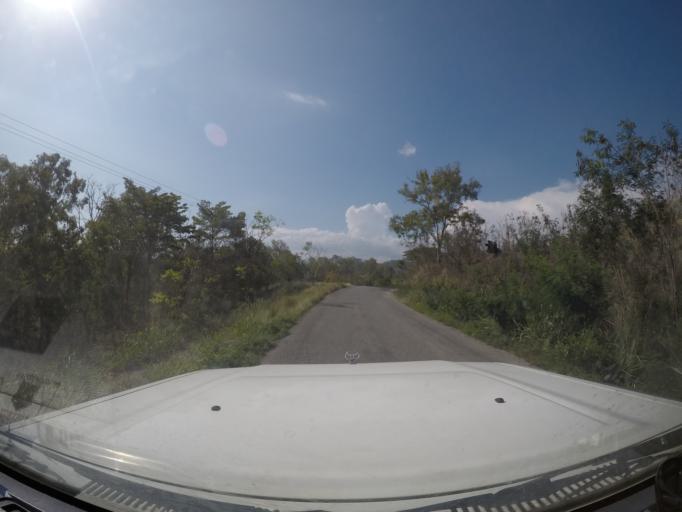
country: PG
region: Central Province
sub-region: Rigo
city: Kwikila
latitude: -9.8657
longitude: 147.5629
